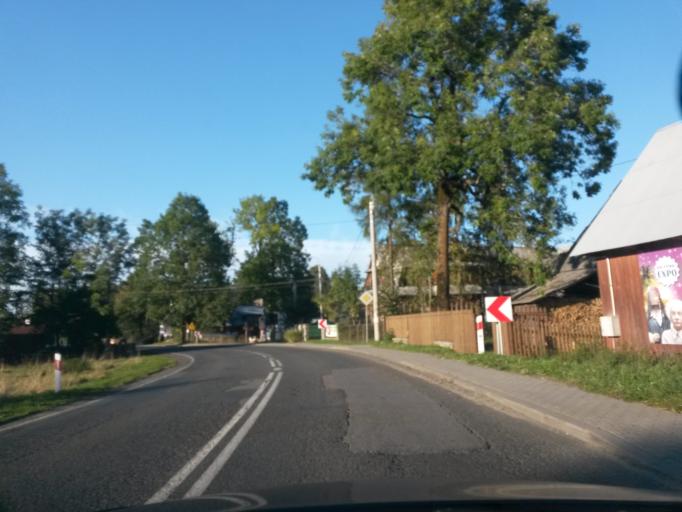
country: PL
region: Lesser Poland Voivodeship
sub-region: Powiat tatrzanski
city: Koscielisko
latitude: 49.3207
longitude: 19.8265
